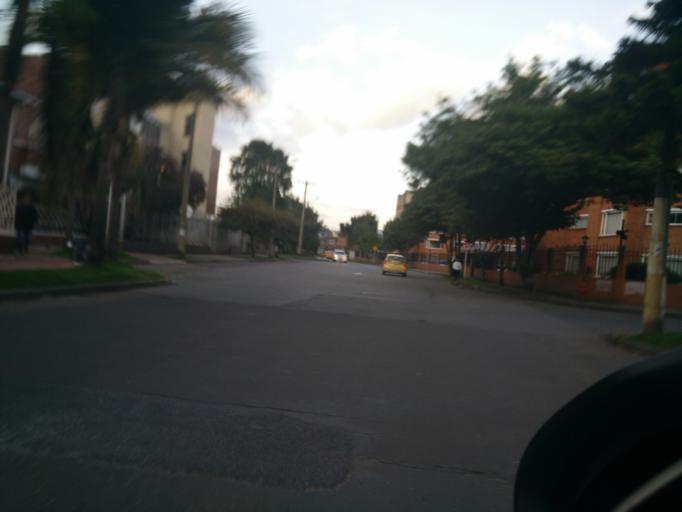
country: CO
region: Bogota D.C.
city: Bogota
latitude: 4.6449
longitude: -74.0896
